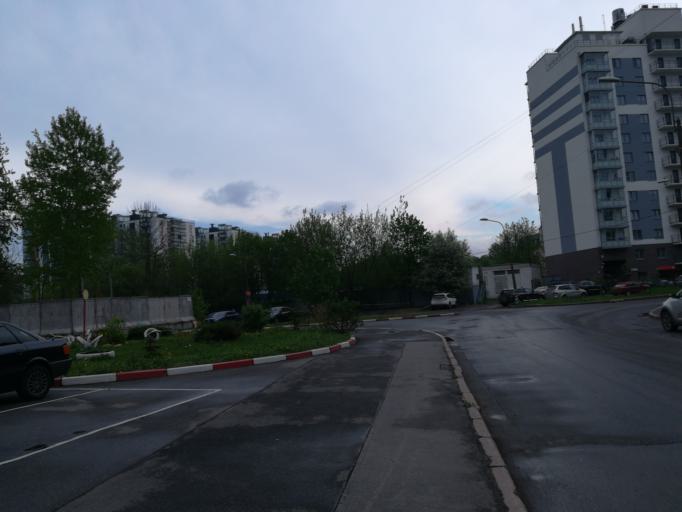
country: RU
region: St.-Petersburg
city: Vasyl'evsky Ostrov
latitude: 59.9508
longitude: 30.2497
